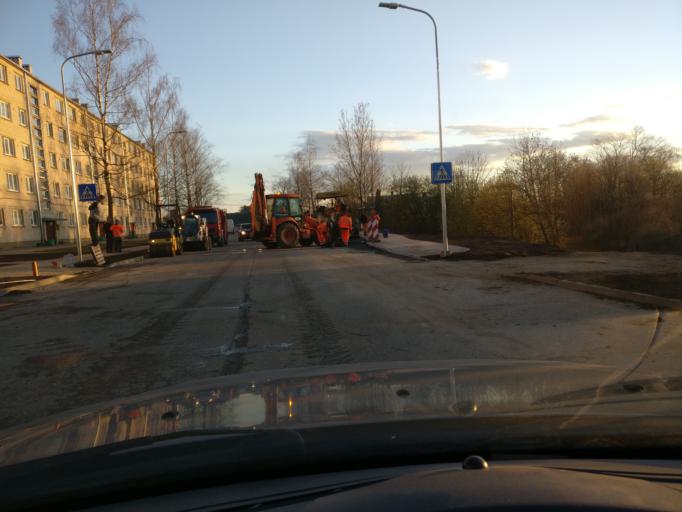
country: LV
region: Aluksnes Rajons
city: Aluksne
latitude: 57.4181
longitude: 27.0634
